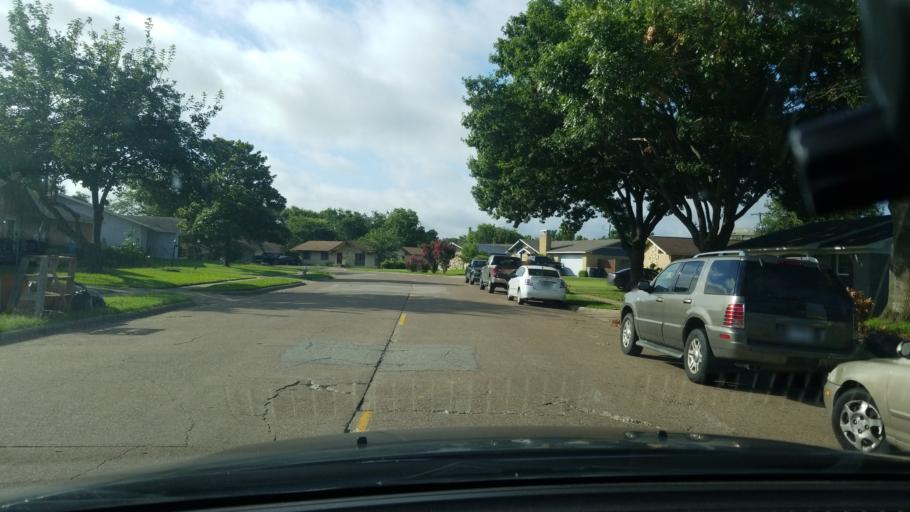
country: US
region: Texas
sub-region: Dallas County
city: Mesquite
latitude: 32.8154
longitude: -96.6867
